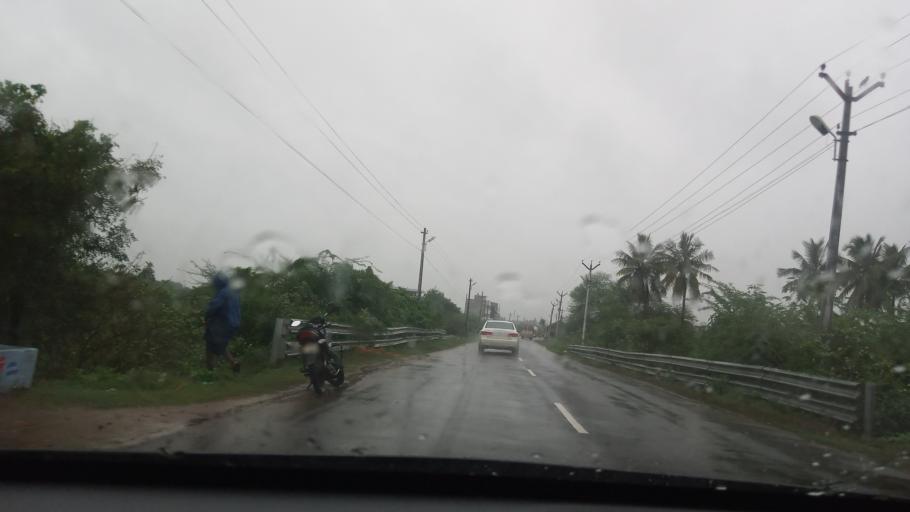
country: IN
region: Tamil Nadu
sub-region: Tiruvannamalai
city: Cheyyar
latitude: 12.6530
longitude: 79.5385
